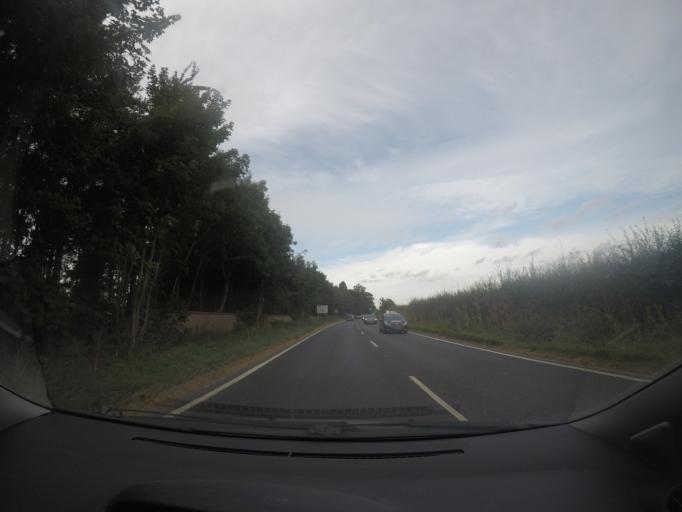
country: GB
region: England
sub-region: City of York
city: Fulford
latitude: 53.9197
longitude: -1.0620
